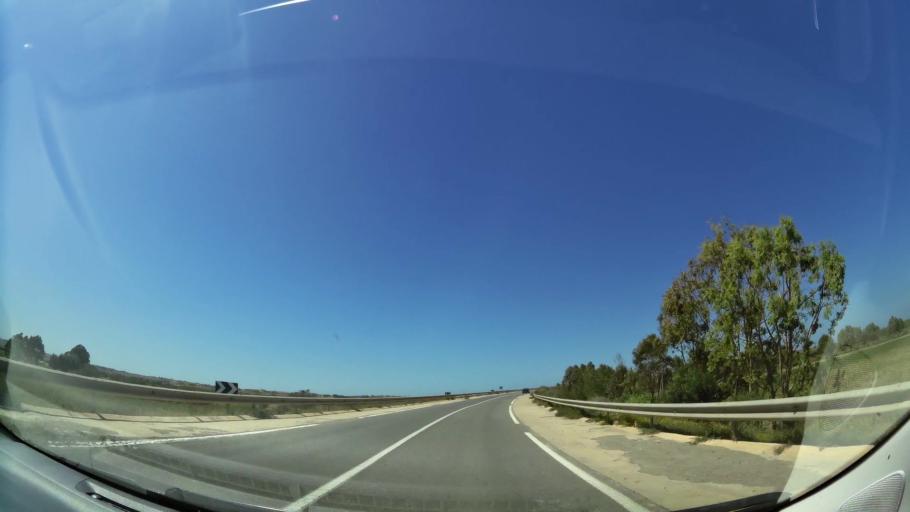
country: MA
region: Oriental
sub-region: Berkane-Taourirt
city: Madagh
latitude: 35.1051
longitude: -2.3603
